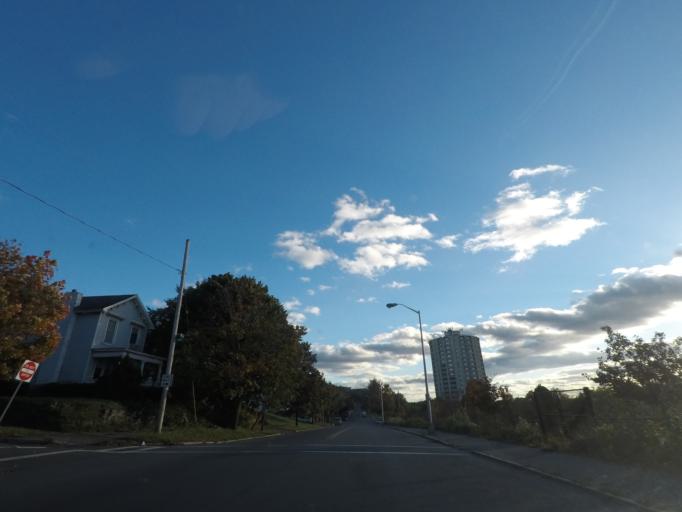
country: US
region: New York
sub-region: Albany County
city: Green Island
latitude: 42.7364
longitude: -73.6826
